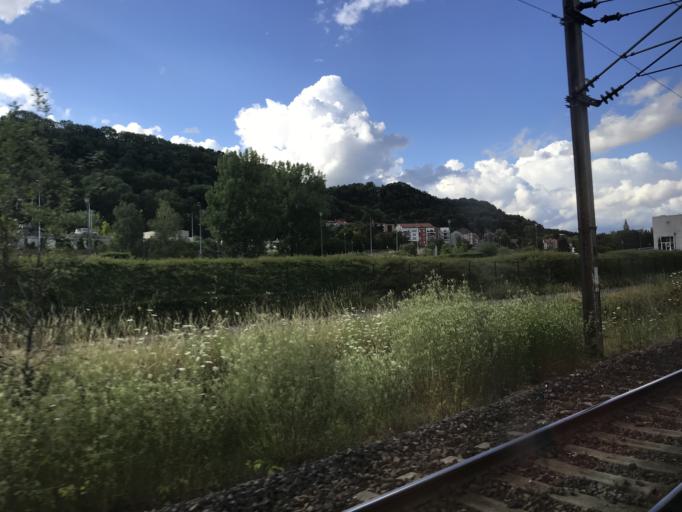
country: FR
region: Lorraine
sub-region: Departement de Meurthe-et-Moselle
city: Longwy
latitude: 49.5225
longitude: 5.7755
